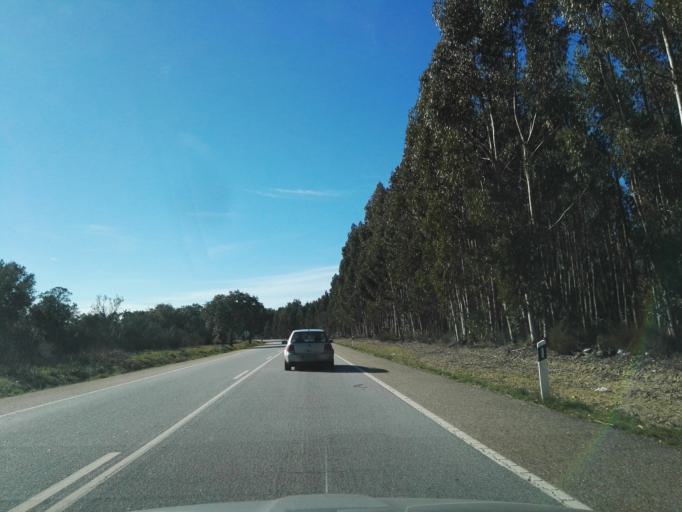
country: PT
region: Portalegre
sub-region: Gaviao
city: Gaviao
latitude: 39.4466
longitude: -7.8117
